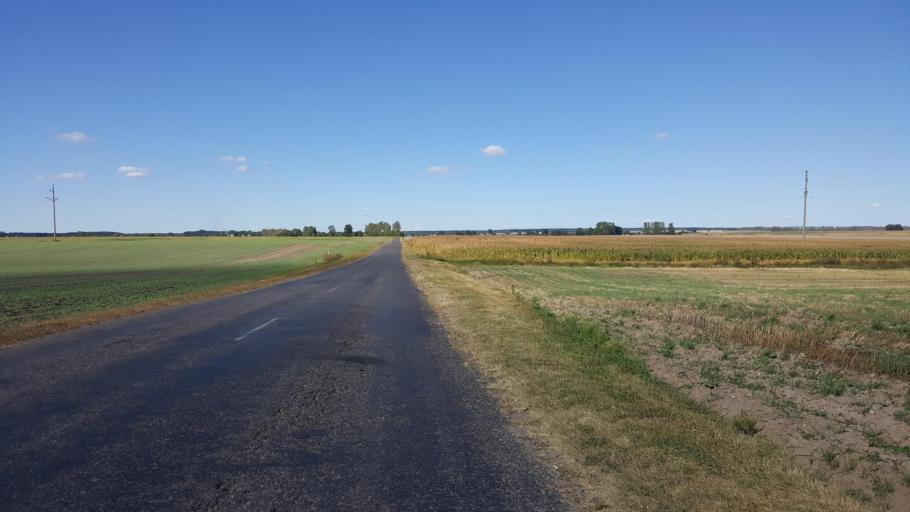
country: BY
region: Brest
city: Vysokaye
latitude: 52.2792
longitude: 23.4858
